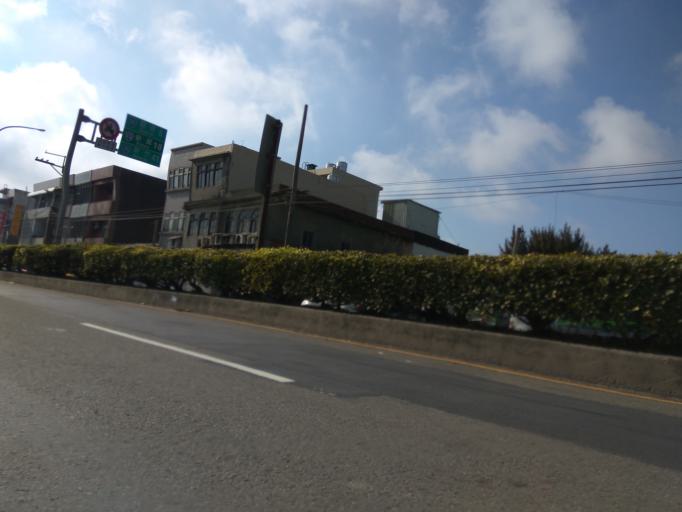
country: TW
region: Taiwan
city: Taoyuan City
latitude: 25.0702
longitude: 121.1964
